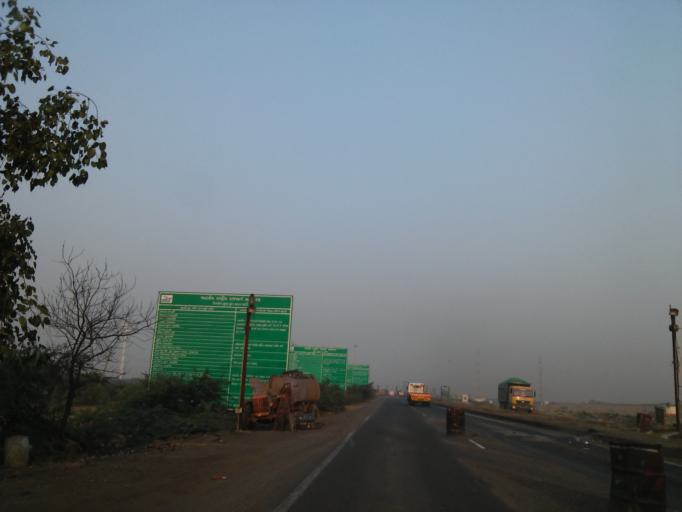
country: IN
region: Gujarat
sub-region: Kachchh
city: Rapar
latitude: 23.2320
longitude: 70.6925
